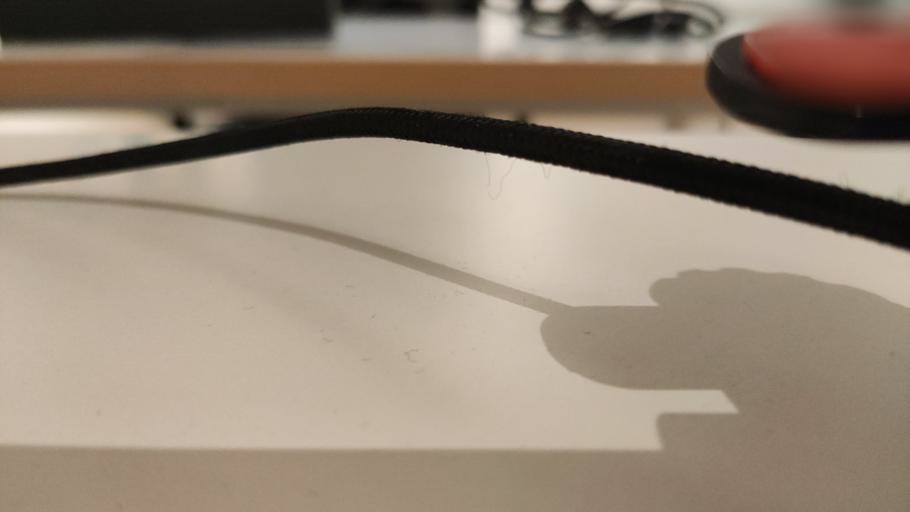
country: RU
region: Kaluga
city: Belousovo
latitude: 55.1454
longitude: 36.7627
